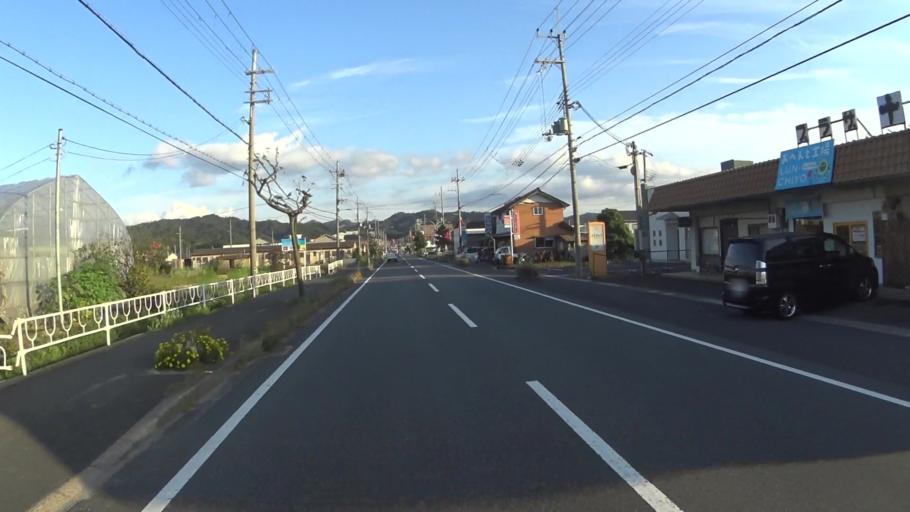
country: JP
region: Kyoto
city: Miyazu
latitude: 35.5900
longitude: 135.0945
